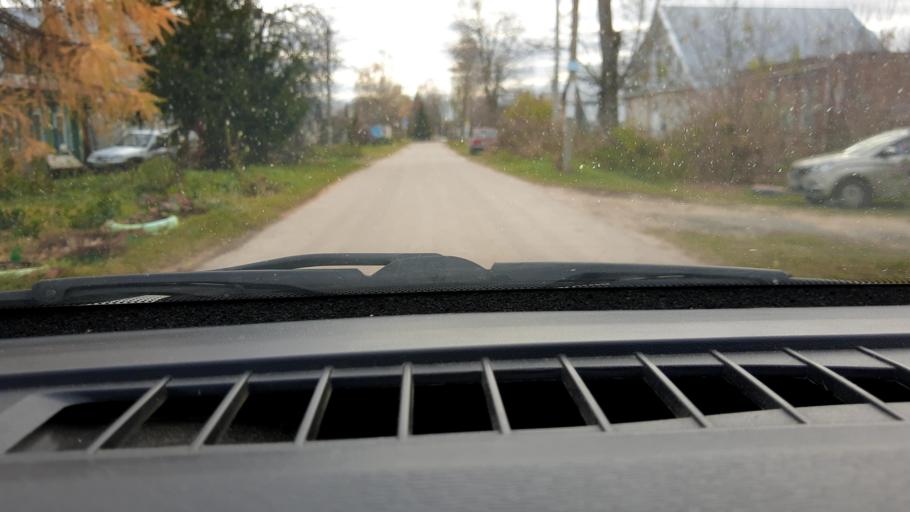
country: RU
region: Nizjnij Novgorod
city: Afonino
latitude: 56.2743
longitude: 44.1066
